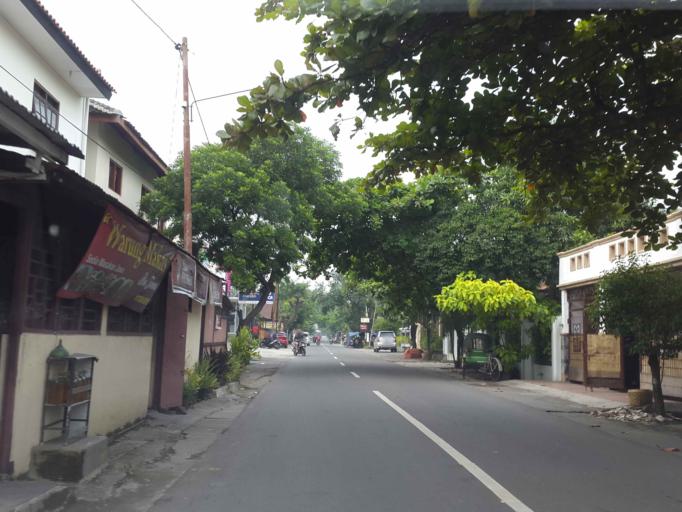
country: ID
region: Central Java
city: Surakarta
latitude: -7.5573
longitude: 110.7908
